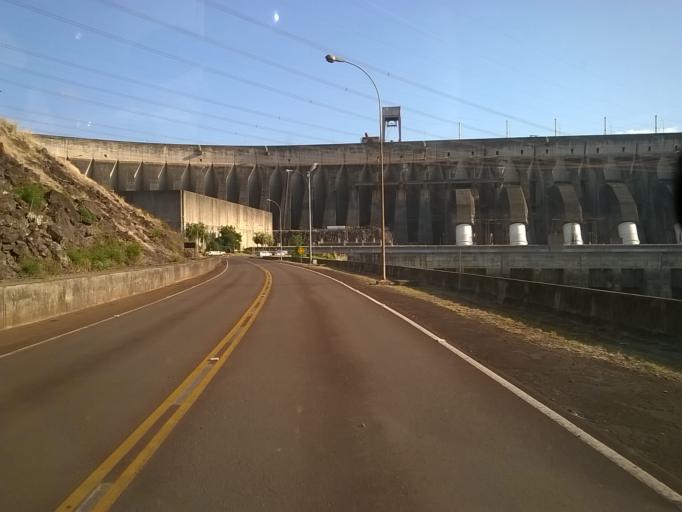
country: PY
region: Alto Parana
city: Ciudad del Este
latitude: -25.4106
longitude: -54.5932
